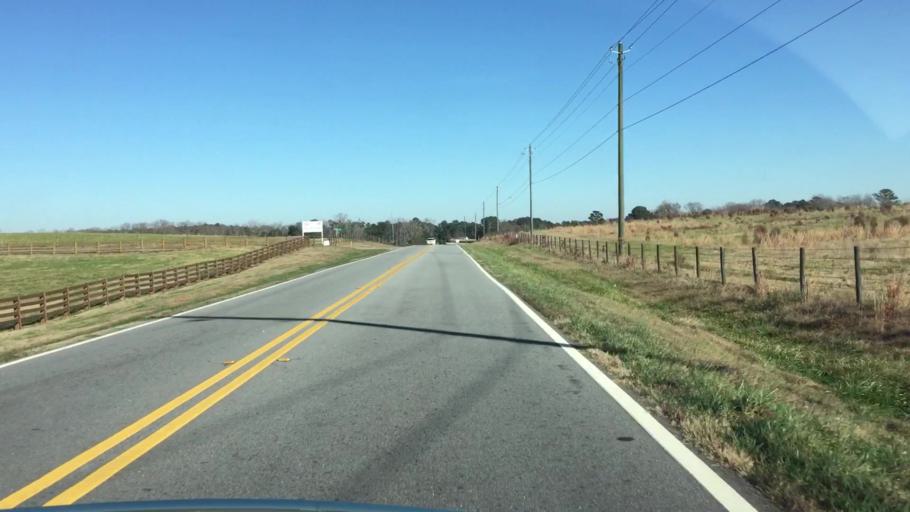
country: US
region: Georgia
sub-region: Henry County
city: McDonough
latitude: 33.5005
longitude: -84.0855
